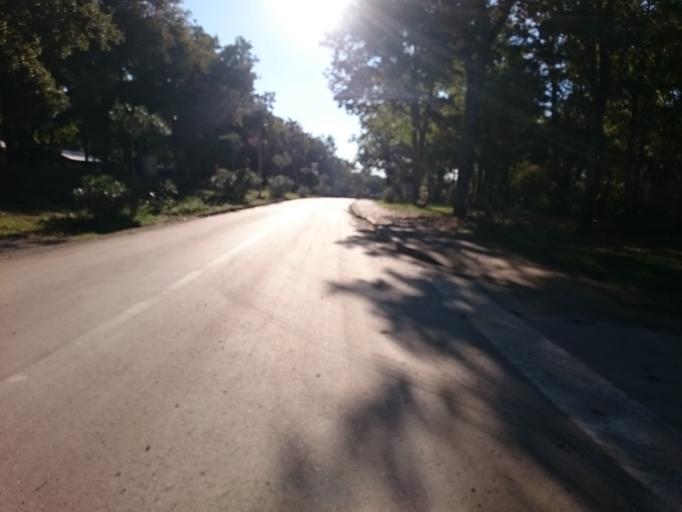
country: HR
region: Istarska
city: Novigrad
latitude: 45.2998
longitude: 13.5928
